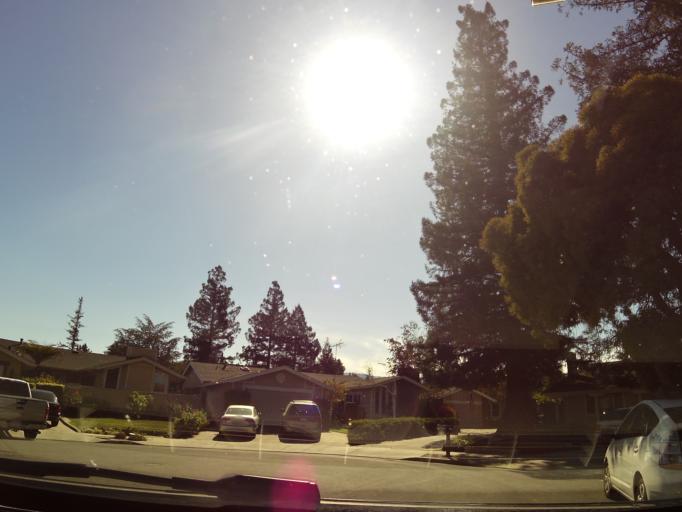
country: US
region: California
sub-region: Santa Clara County
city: Campbell
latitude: 37.2687
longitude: -121.9707
